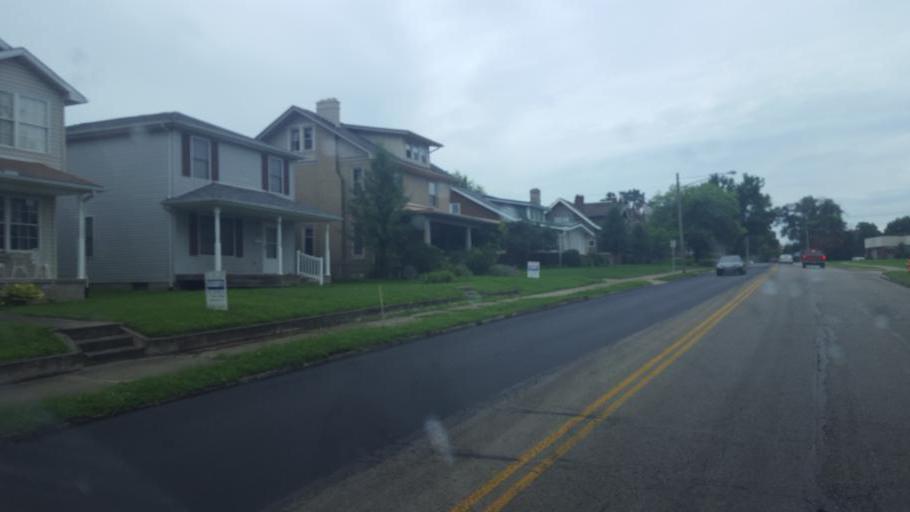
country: US
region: Ohio
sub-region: Pickaway County
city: Circleville
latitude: 39.6085
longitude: -82.9419
